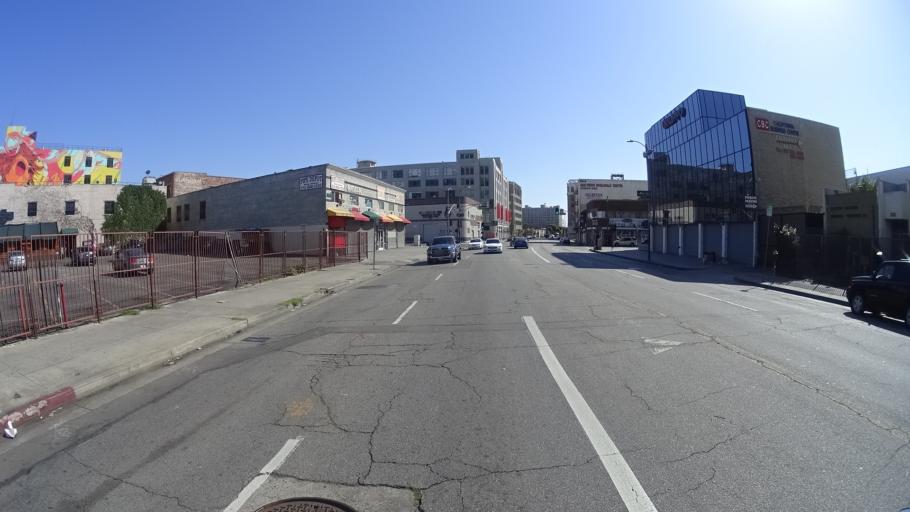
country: US
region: California
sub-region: Los Angeles County
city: Los Angeles
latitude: 34.0465
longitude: -118.2428
